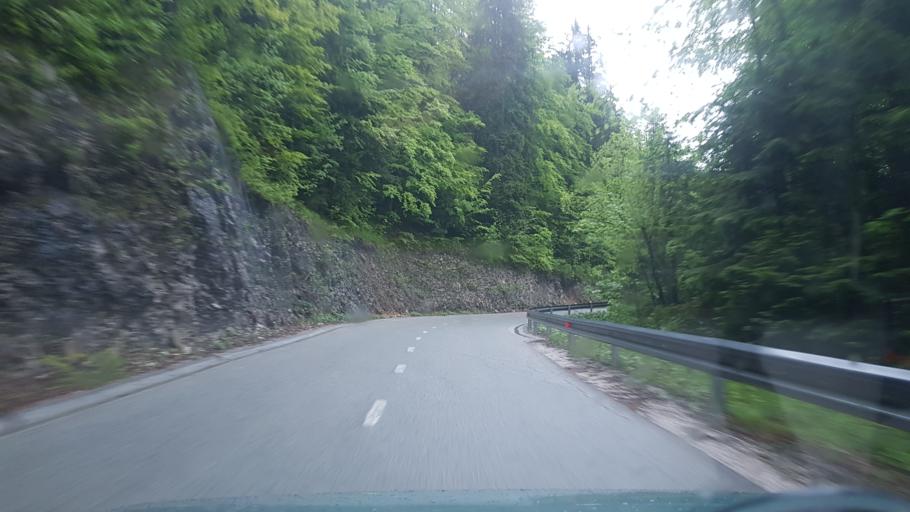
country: SI
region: Bohinj
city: Bohinjska Bistrica
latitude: 46.2605
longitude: 14.0083
